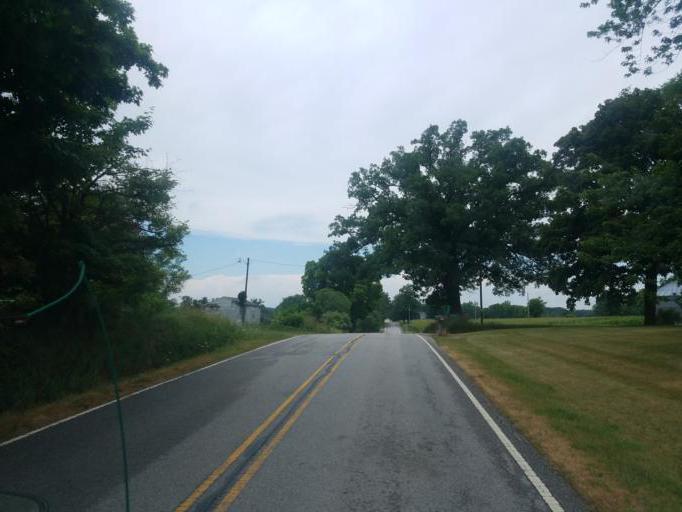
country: US
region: Indiana
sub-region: DeKalb County
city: Butler
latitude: 41.3865
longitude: -84.8381
